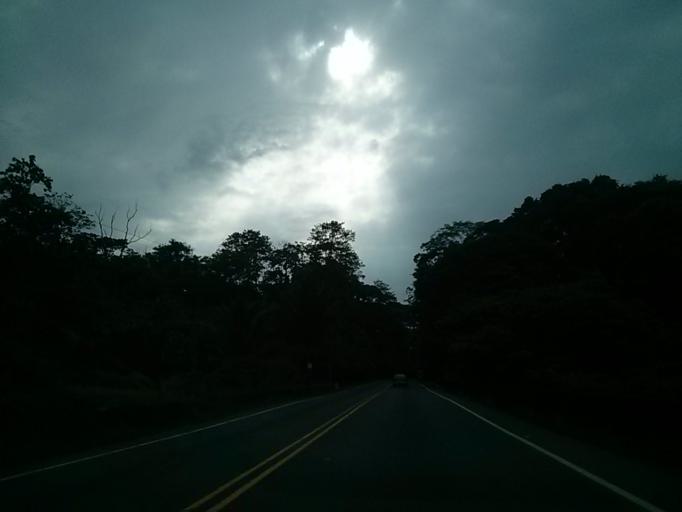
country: CR
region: Limon
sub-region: Canton de Pococi
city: Guapiles
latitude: 10.2033
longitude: -83.8164
